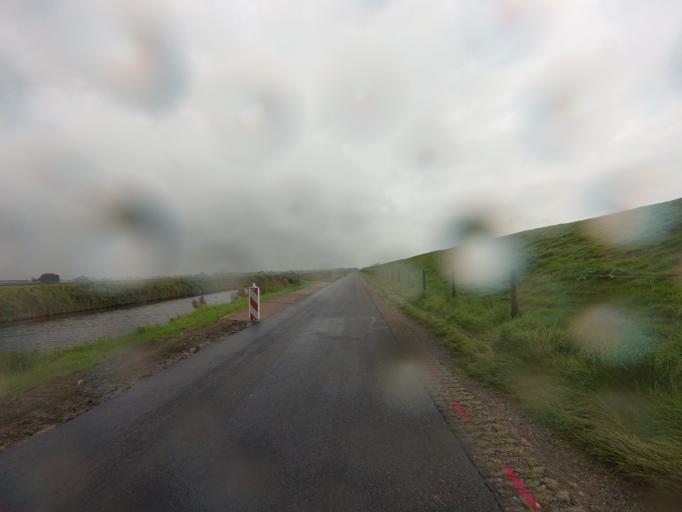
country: NL
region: Friesland
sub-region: Sudwest Fryslan
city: Koudum
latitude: 52.9189
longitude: 5.4106
